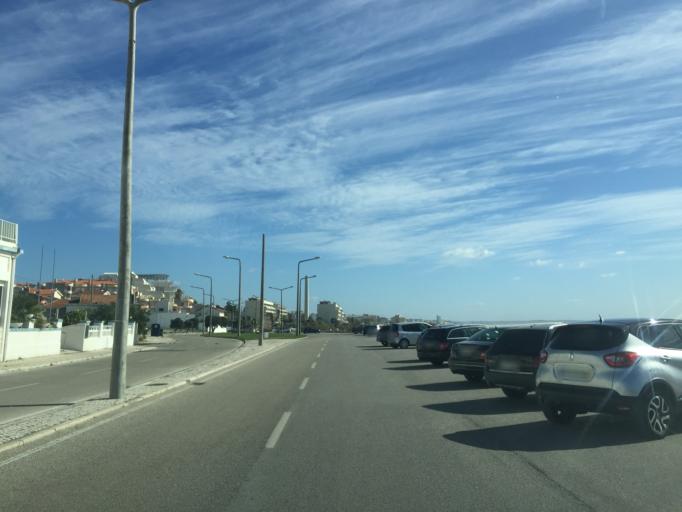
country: PT
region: Coimbra
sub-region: Figueira da Foz
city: Buarcos
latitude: 40.1766
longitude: -8.8984
